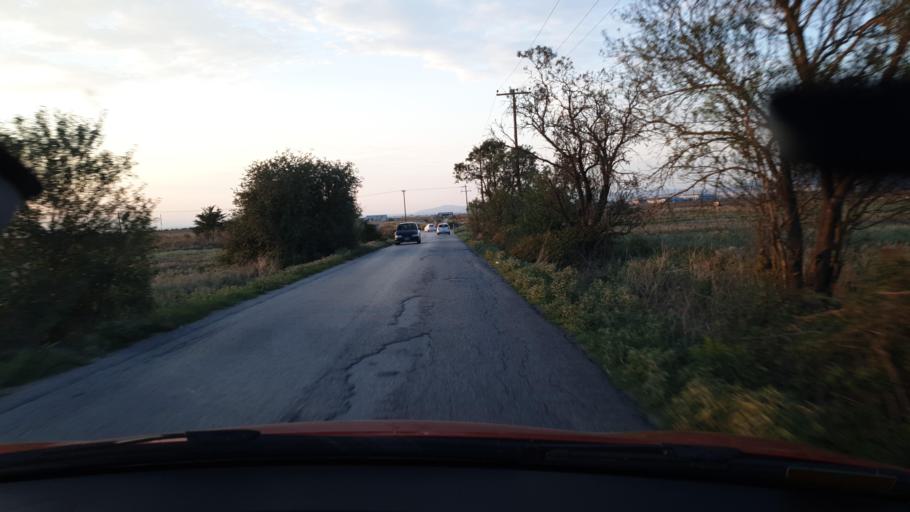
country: GR
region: Central Macedonia
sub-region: Nomos Thessalonikis
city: Peraia
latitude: 40.5067
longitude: 22.9481
